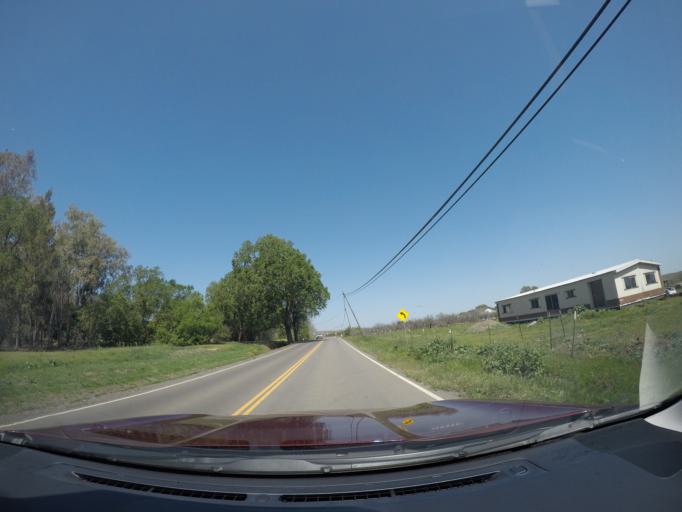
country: US
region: California
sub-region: Yolo County
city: Winters
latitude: 38.4919
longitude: -121.9503
